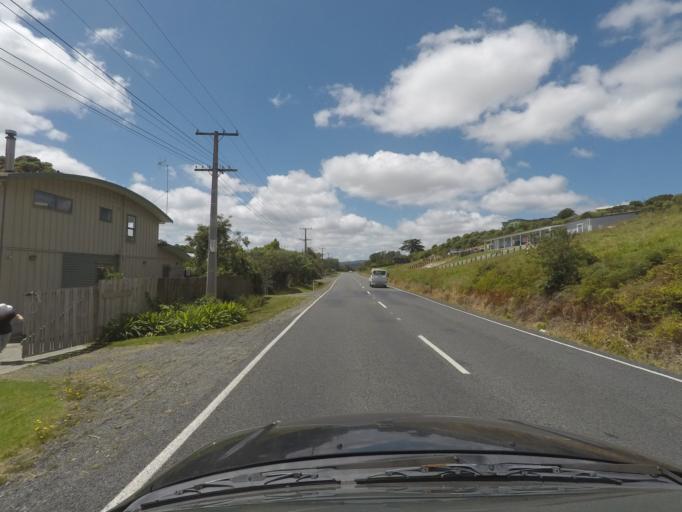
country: NZ
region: Northland
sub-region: Whangarei
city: Ruakaka
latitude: -35.9942
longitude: 174.4711
